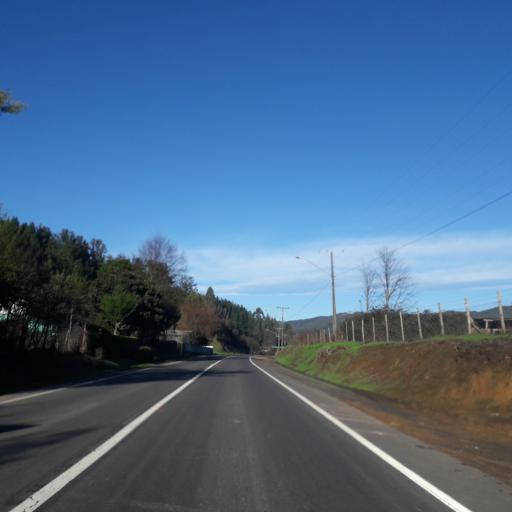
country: CL
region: Biobio
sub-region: Provincia de Concepcion
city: Lota
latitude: -37.2056
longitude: -72.9525
